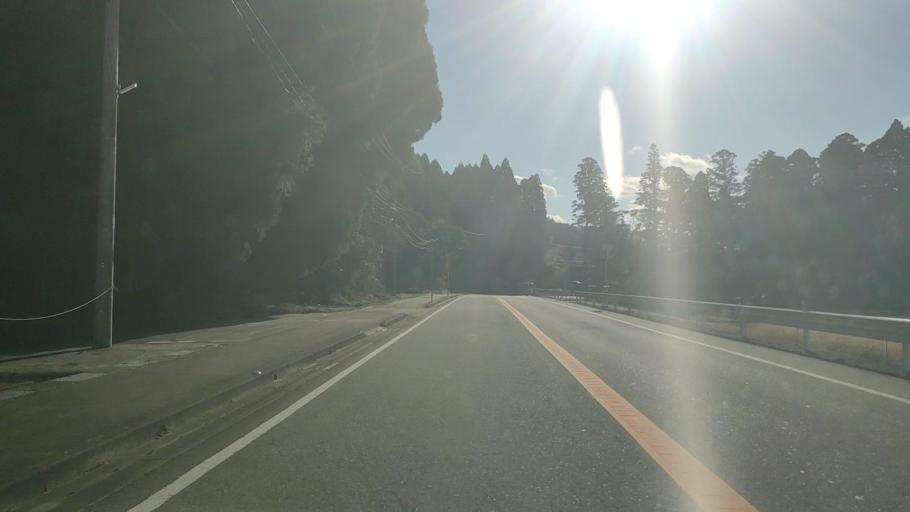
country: JP
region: Fukuoka
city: Maebaru-chuo
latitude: 33.4459
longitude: 130.2714
